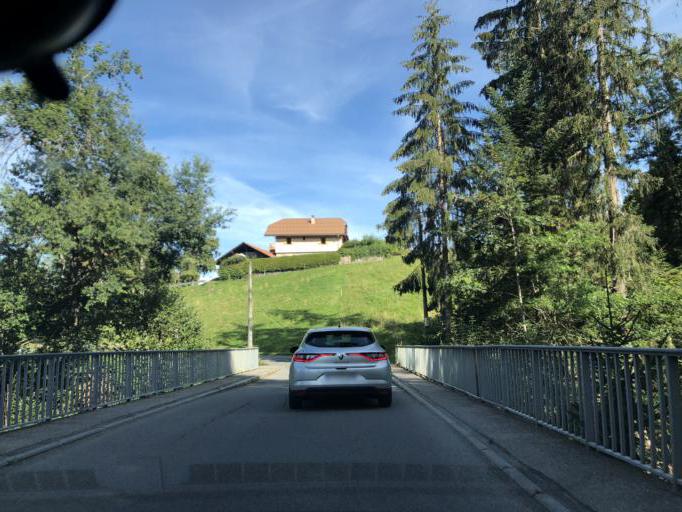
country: FR
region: Rhone-Alpes
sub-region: Departement de la Haute-Savoie
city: Cordon
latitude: 45.9132
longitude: 6.6104
